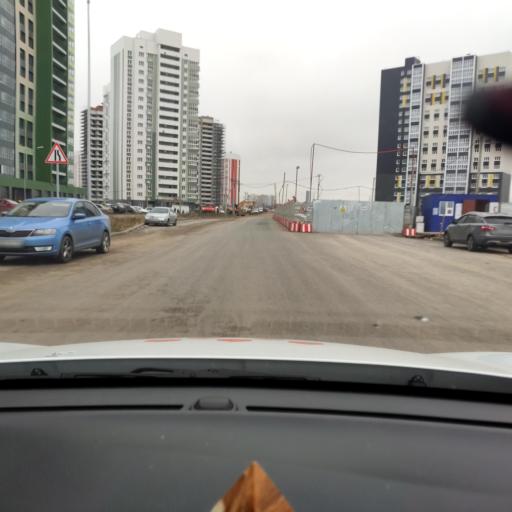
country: RU
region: Tatarstan
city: Osinovo
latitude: 55.8577
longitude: 48.9056
